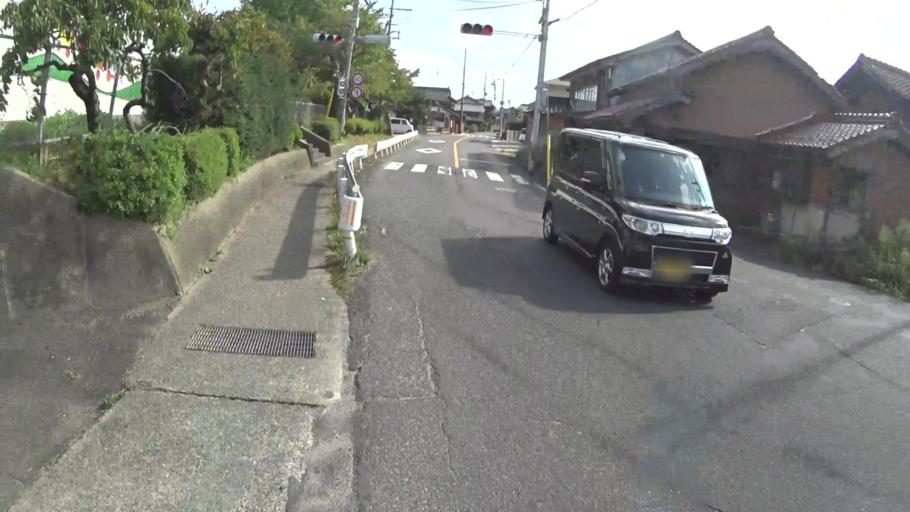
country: JP
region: Kyoto
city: Miyazu
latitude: 35.6134
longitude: 135.0836
